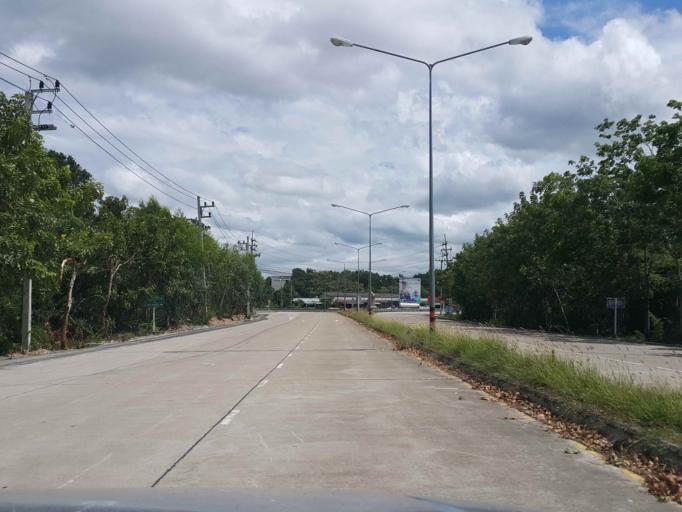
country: TH
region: Tak
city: Tak
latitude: 16.8552
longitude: 99.1170
